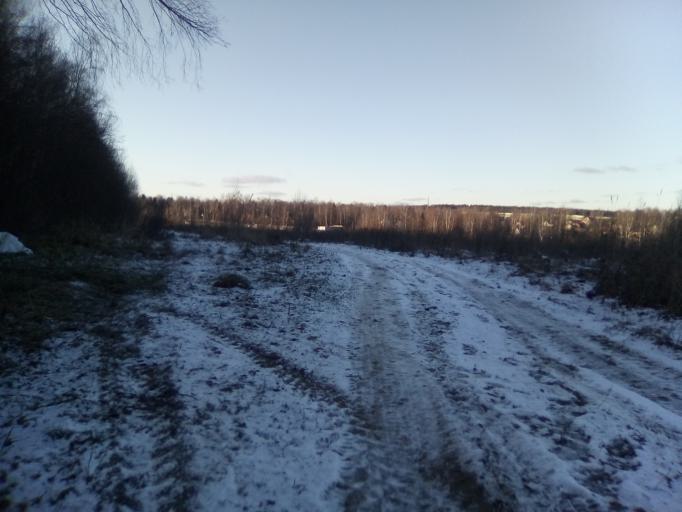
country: RU
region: Moskovskaya
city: Lesnoy Gorodok
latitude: 55.6491
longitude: 37.1788
